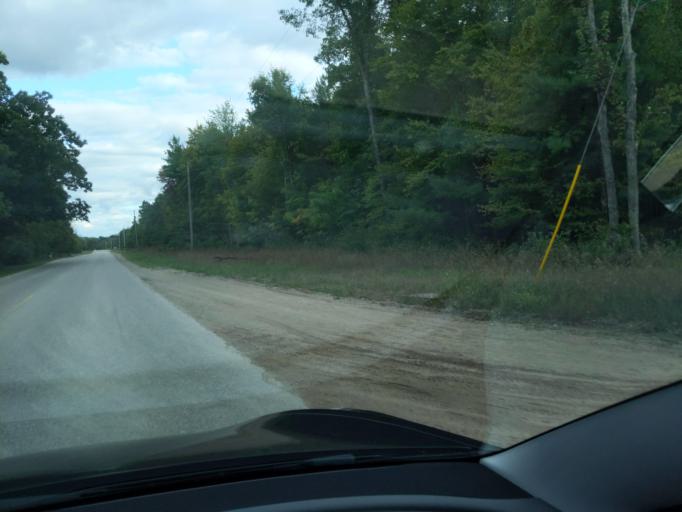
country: US
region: Michigan
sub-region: Kalkaska County
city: Rapid City
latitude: 44.8380
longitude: -85.2929
